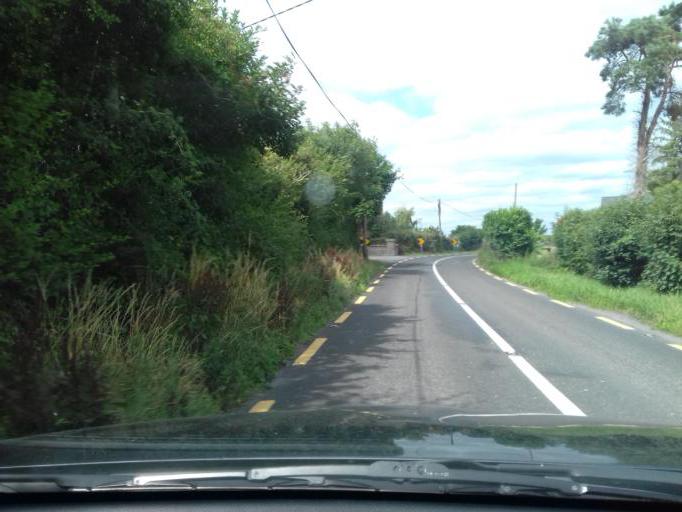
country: IE
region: Leinster
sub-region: County Carlow
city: Tullow
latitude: 52.8537
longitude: -6.7102
